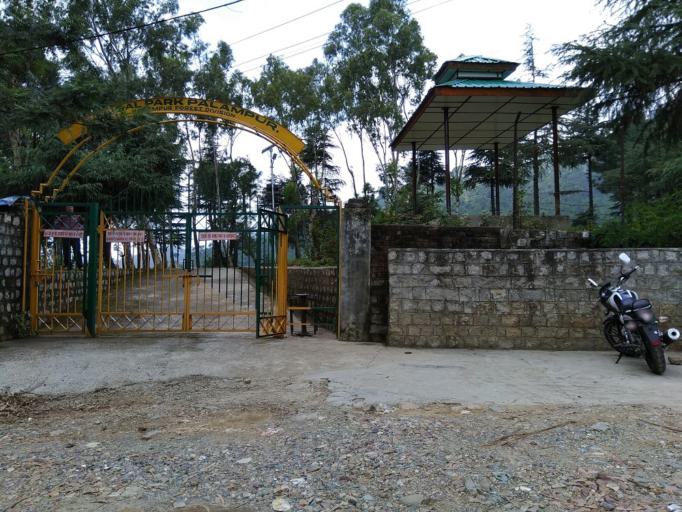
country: IN
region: Himachal Pradesh
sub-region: Kangra
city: Palampur
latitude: 32.1250
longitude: 76.5294
